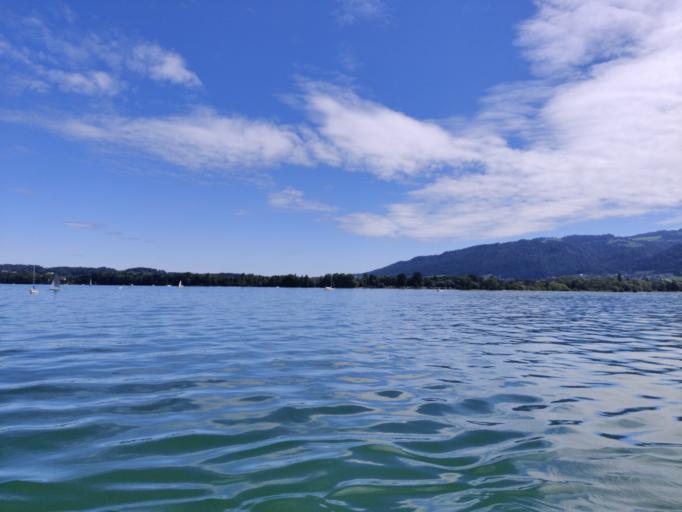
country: AT
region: Vorarlberg
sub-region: Politischer Bezirk Bregenz
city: Lochau
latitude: 47.5298
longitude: 9.7180
